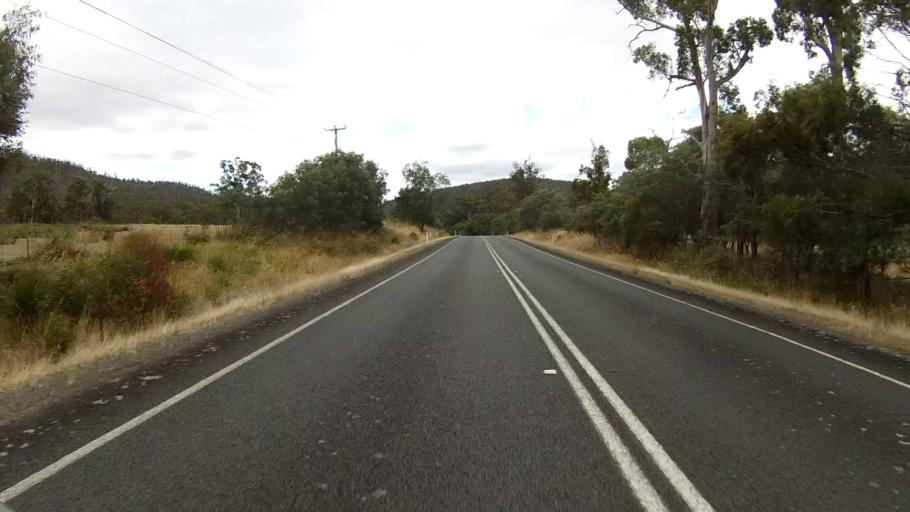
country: AU
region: Tasmania
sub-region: Sorell
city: Sorell
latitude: -42.5807
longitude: 147.8146
